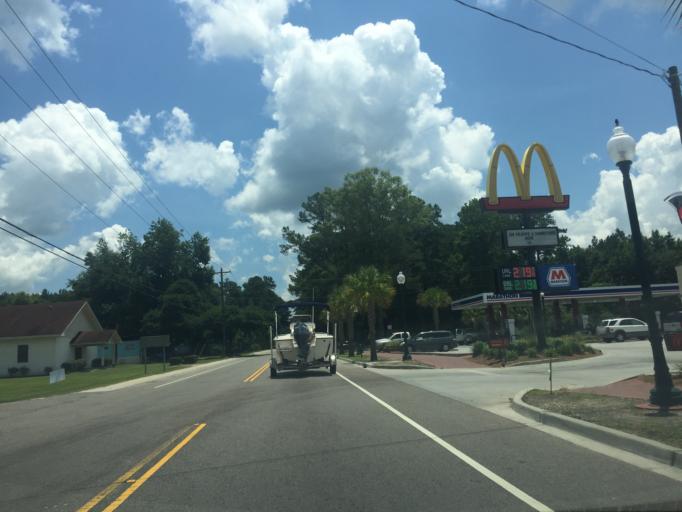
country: US
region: South Carolina
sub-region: Jasper County
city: Ridgeland
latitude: 32.4767
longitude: -80.9691
